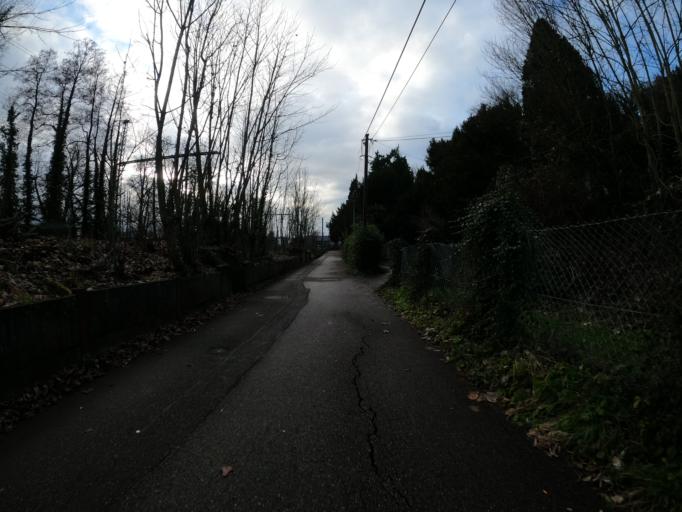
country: DE
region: Baden-Wuerttemberg
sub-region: Regierungsbezirk Stuttgart
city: Schwabisch Gmund
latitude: 48.8026
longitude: 9.7942
